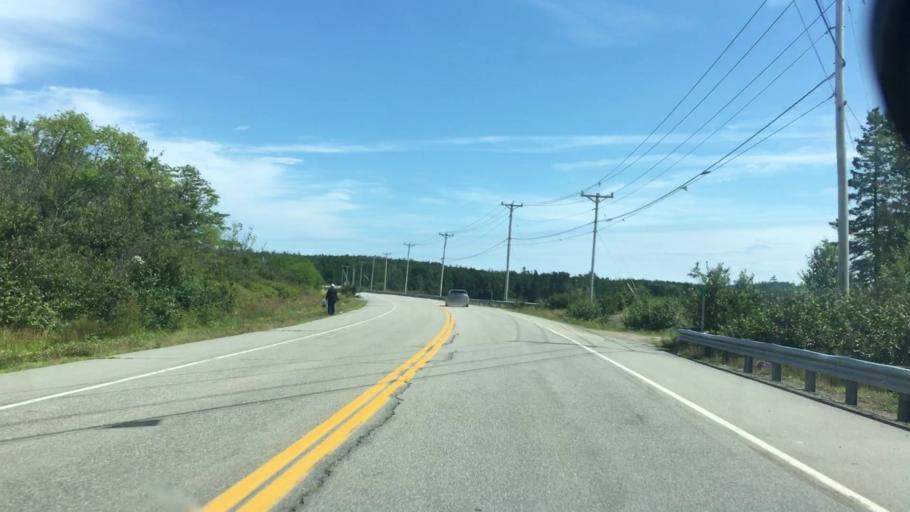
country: US
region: Maine
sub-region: Washington County
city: Eastport
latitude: 44.9397
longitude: -67.0352
